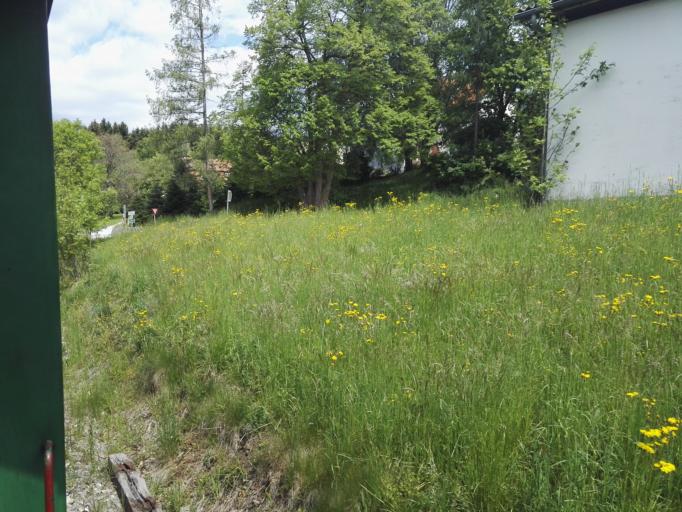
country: AT
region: Styria
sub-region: Politischer Bezirk Weiz
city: Anger
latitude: 47.2753
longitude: 15.6970
